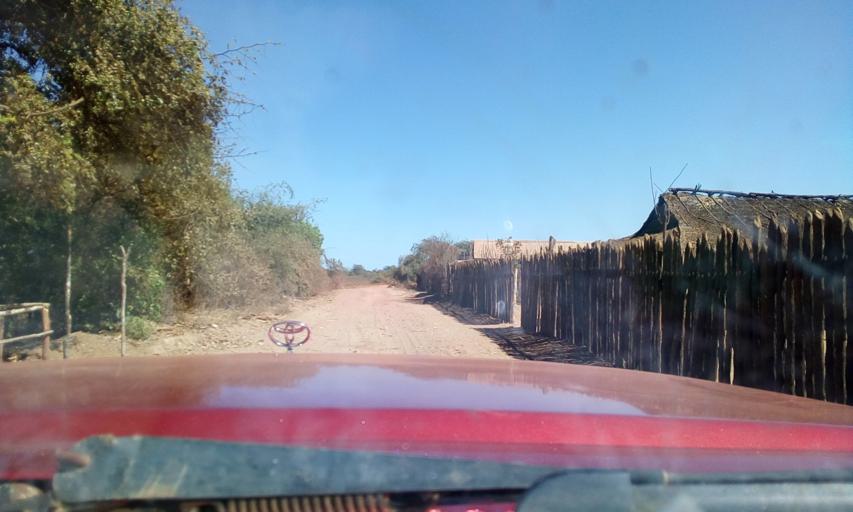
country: MG
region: Boeny
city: Mahajanga
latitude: -15.9623
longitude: 45.9446
